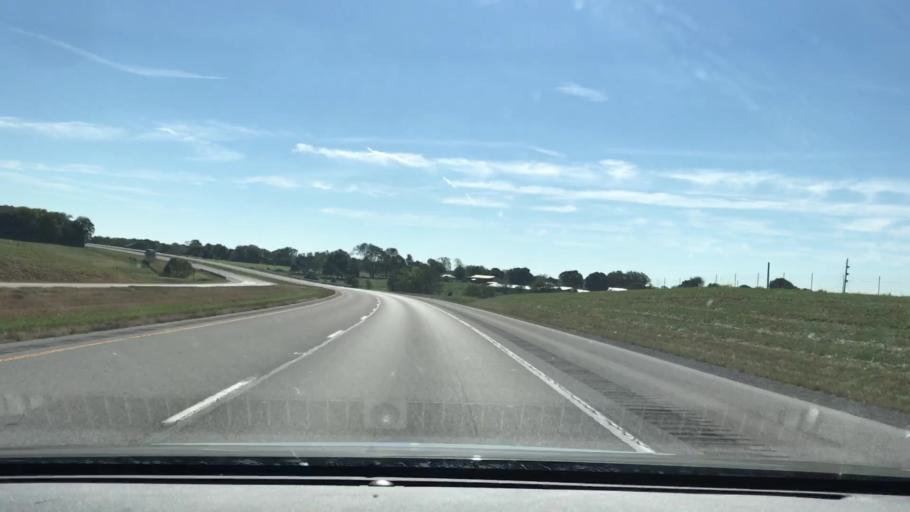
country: US
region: Kentucky
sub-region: Todd County
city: Elkton
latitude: 36.8127
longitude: -87.1388
